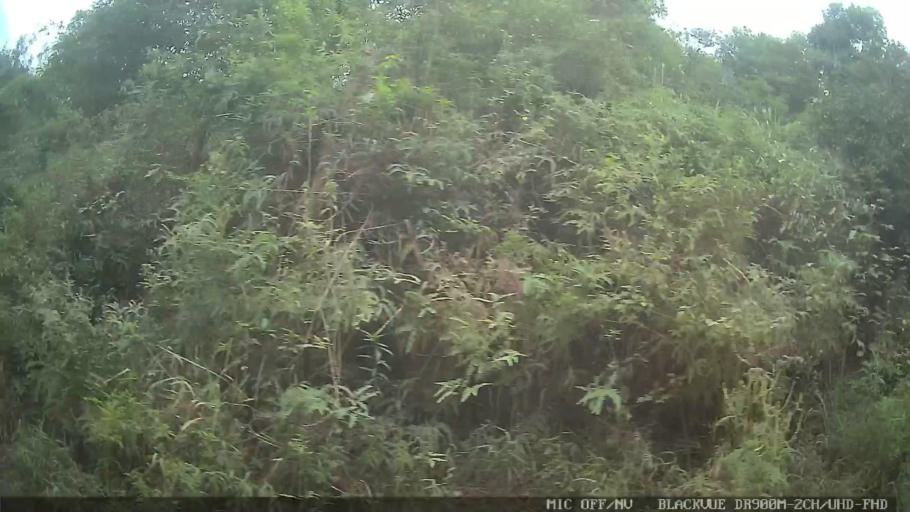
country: BR
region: Sao Paulo
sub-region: Bom Jesus Dos Perdoes
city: Bom Jesus dos Perdoes
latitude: -23.1720
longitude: -46.5137
